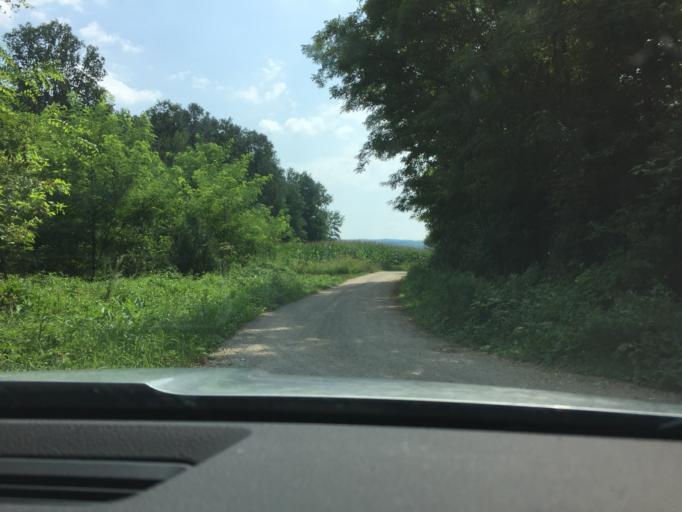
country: SI
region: Metlika
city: Metlika
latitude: 45.6534
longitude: 15.3464
